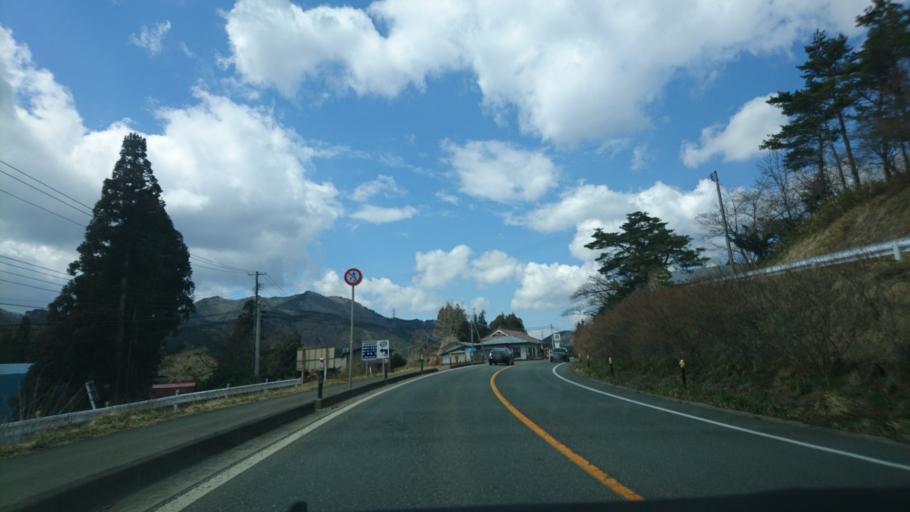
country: JP
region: Iwate
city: Tono
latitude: 39.3029
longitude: 141.3793
